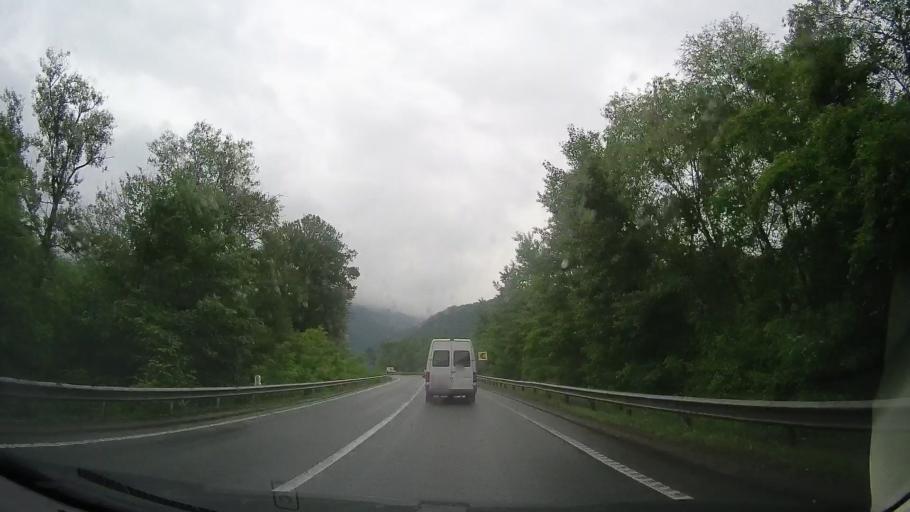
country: RO
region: Caras-Severin
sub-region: Comuna Toplet
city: Toplet
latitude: 44.8412
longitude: 22.3839
